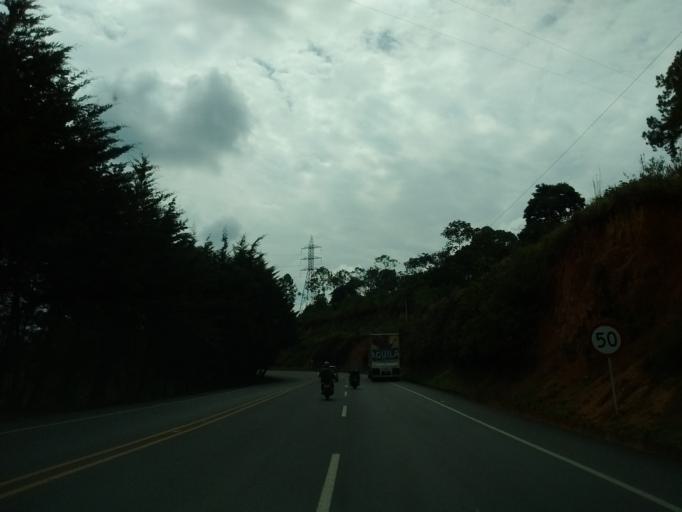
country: CO
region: Cauca
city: Morales
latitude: 2.7207
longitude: -76.5440
